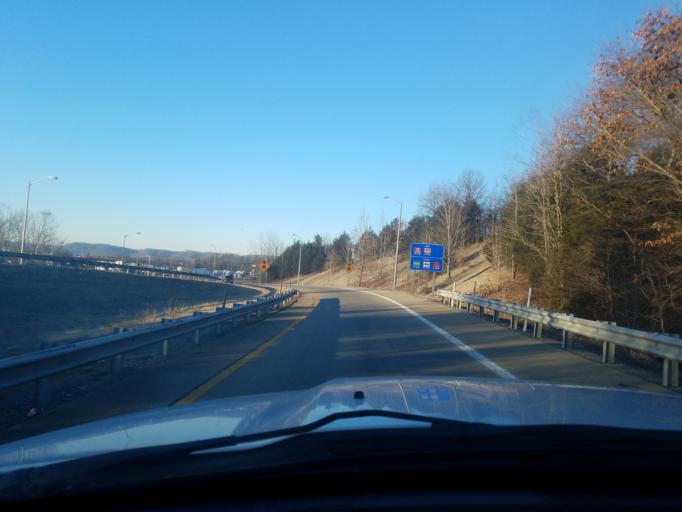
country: US
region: Kentucky
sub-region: Bullitt County
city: Lebanon Junction
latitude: 37.8297
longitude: -85.7214
